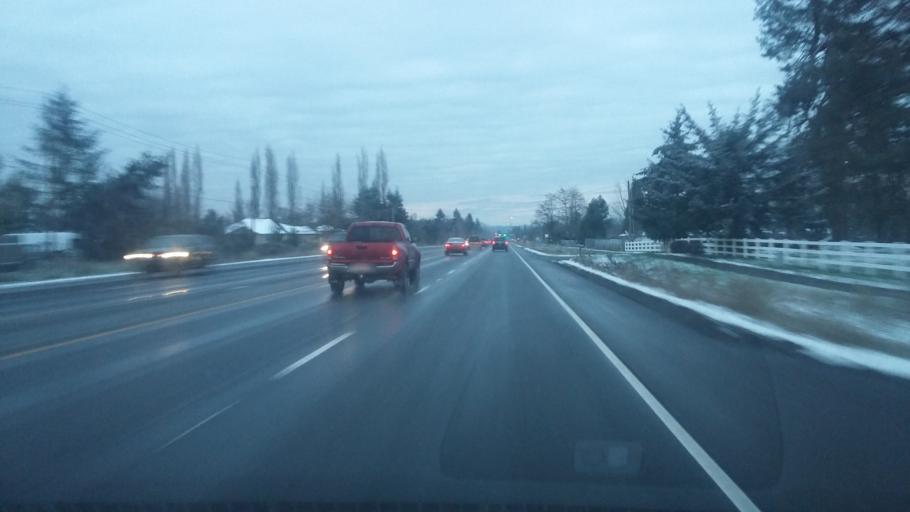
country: US
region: Washington
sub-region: Clark County
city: Meadow Glade
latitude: 45.7605
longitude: -122.5473
